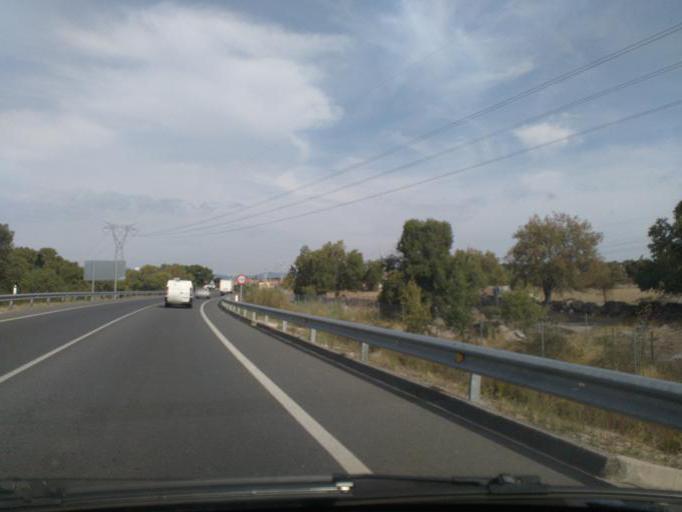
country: ES
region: Madrid
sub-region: Provincia de Madrid
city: Galapagar
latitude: 40.5781
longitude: -3.9905
